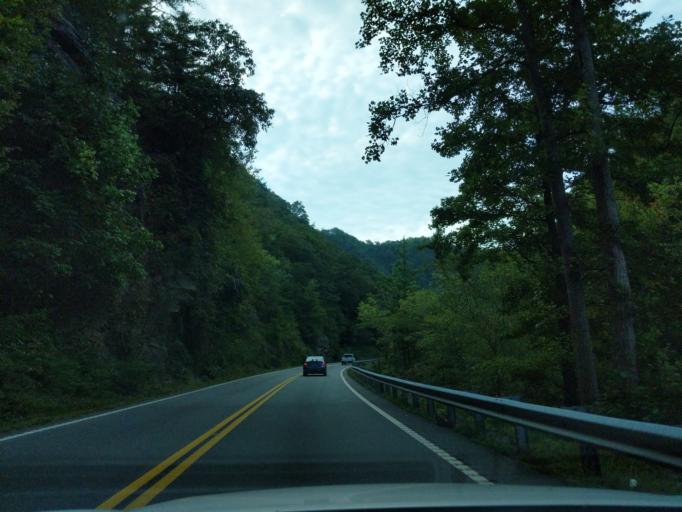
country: US
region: Tennessee
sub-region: Polk County
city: Benton
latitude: 35.0833
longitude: -84.5112
